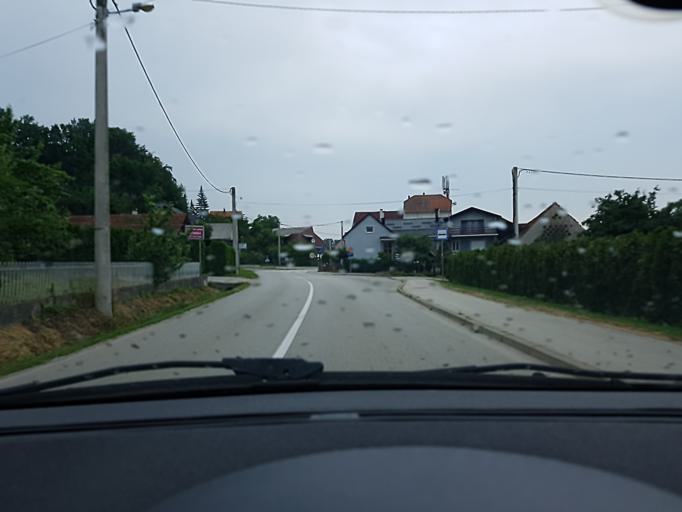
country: HR
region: Zagrebacka
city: Pojatno
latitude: 45.9036
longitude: 15.8018
